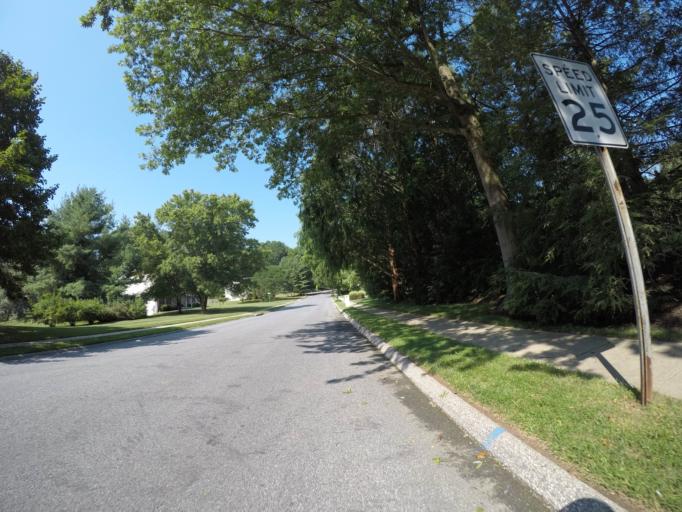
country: US
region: Maryland
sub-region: Howard County
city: Columbia
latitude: 39.2648
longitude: -76.8590
